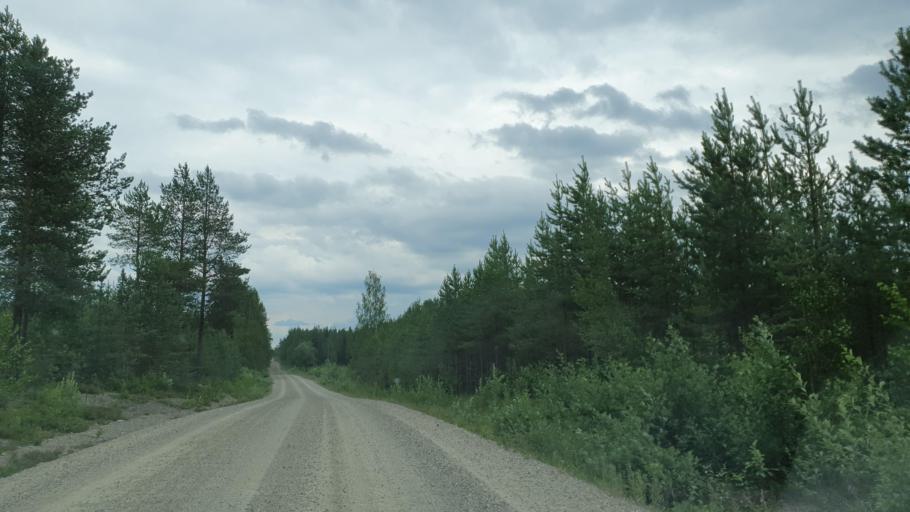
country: RU
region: Republic of Karelia
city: Kostomuksha
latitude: 64.7524
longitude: 29.8868
